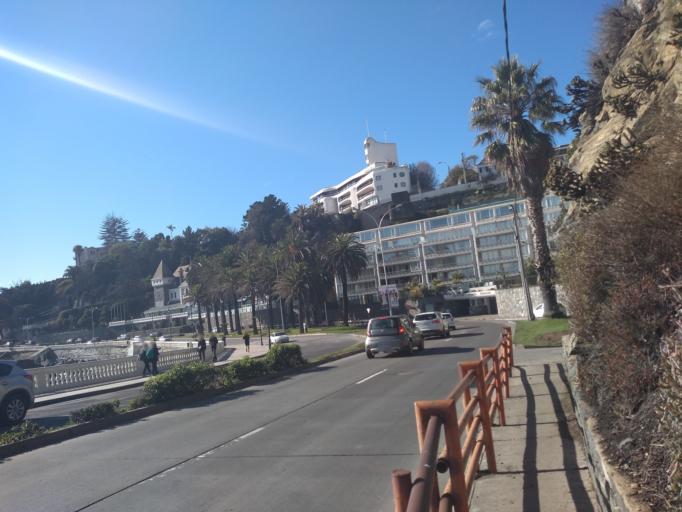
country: CL
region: Valparaiso
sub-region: Provincia de Valparaiso
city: Vina del Mar
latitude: -33.0211
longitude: -71.5671
